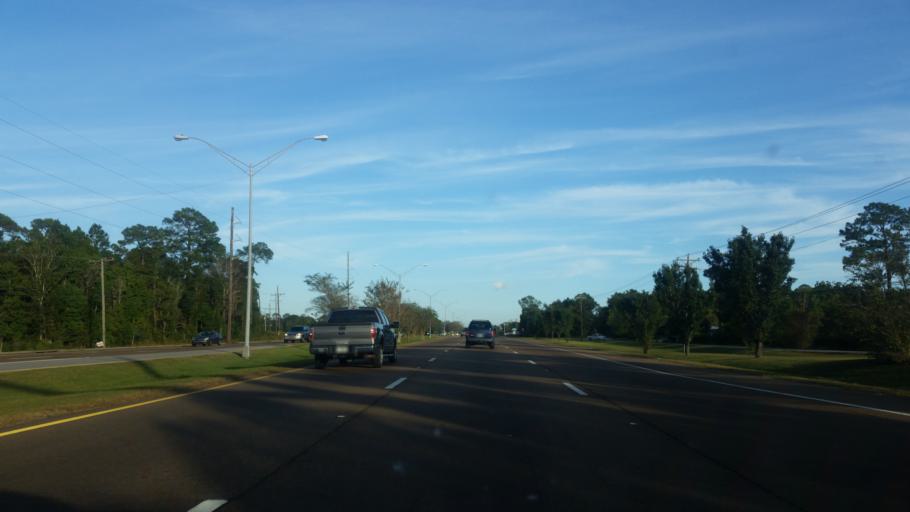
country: US
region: Mississippi
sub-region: Jackson County
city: Gautier
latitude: 30.3884
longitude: -88.6329
